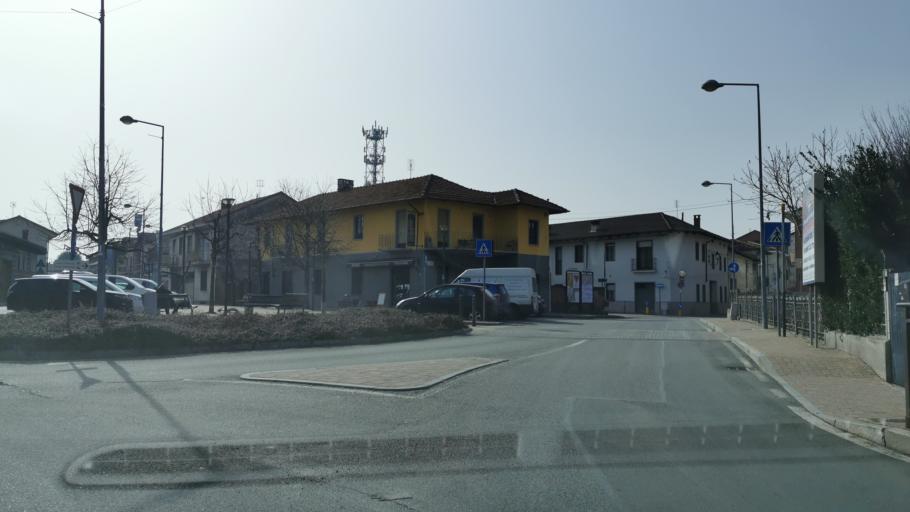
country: IT
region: Piedmont
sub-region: Provincia di Torino
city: Volpiano
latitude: 45.2043
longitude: 7.7796
